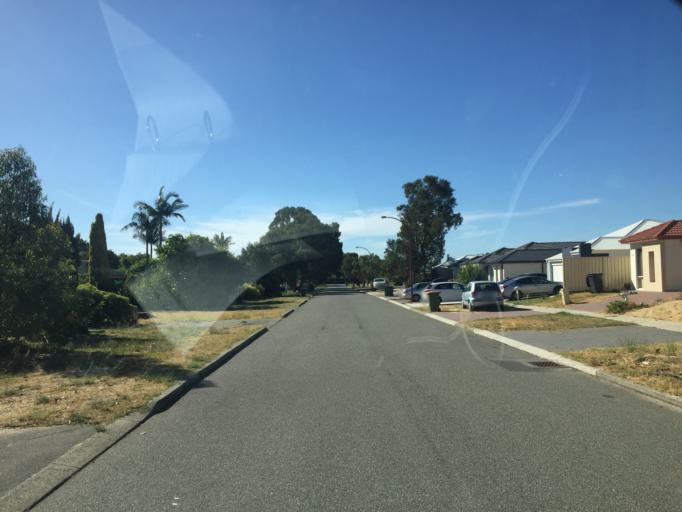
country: AU
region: Western Australia
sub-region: Gosnells
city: Maddington
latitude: -32.0588
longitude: 116.0026
